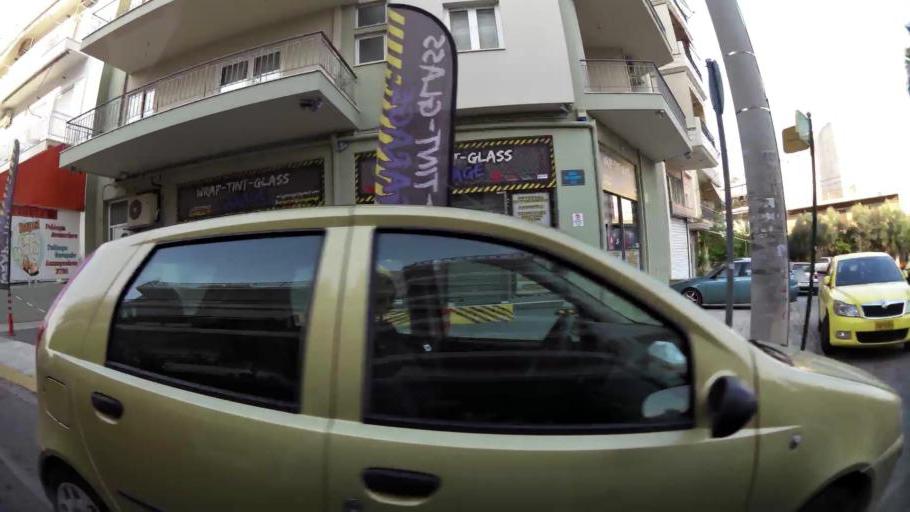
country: GR
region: Attica
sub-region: Nomarchia Athinas
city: Petroupolis
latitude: 38.0387
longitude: 23.6733
